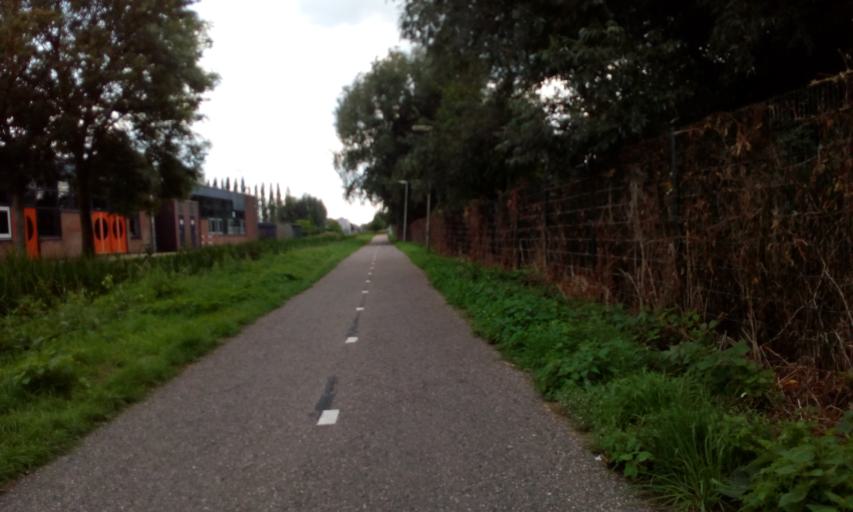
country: NL
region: South Holland
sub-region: Gemeente Waddinxveen
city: Waddinxveen
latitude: 52.0386
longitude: 4.6500
